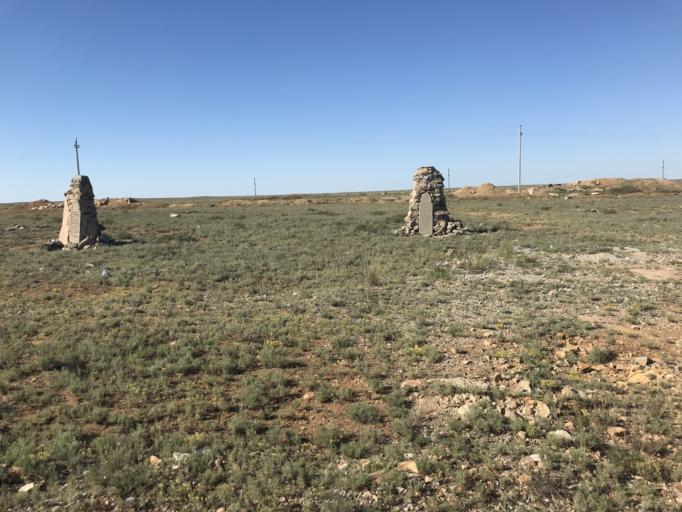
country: RU
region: Orenburg
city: Dombarovskiy
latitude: 50.0825
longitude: 59.5690
